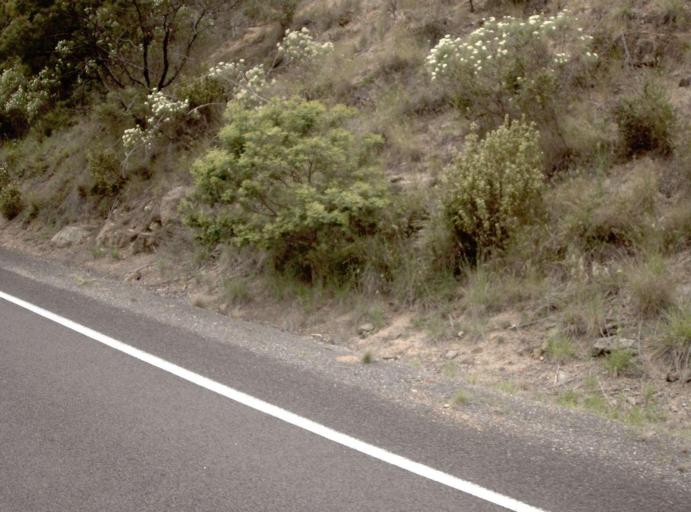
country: AU
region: New South Wales
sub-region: Bombala
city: Bombala
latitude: -37.2504
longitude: 149.2518
